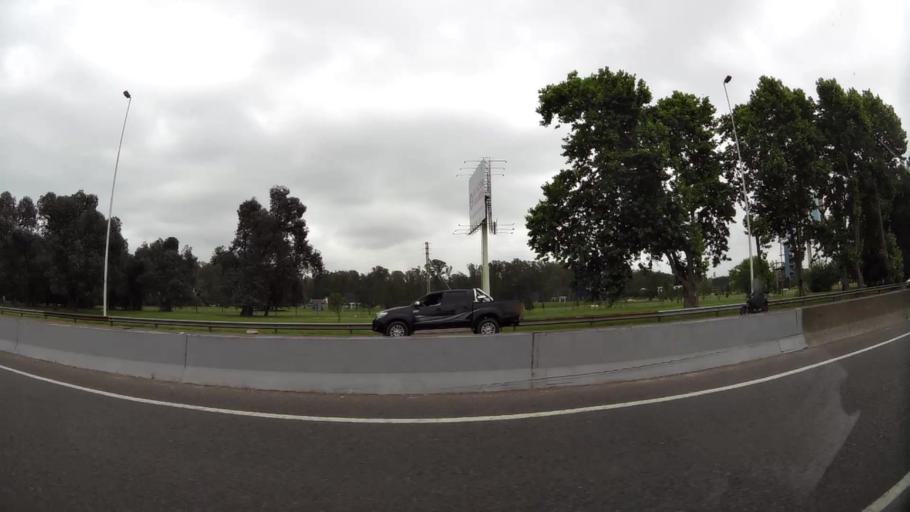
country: AR
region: Buenos Aires
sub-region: Partido de Ezeiza
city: Ezeiza
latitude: -34.7788
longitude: -58.5245
